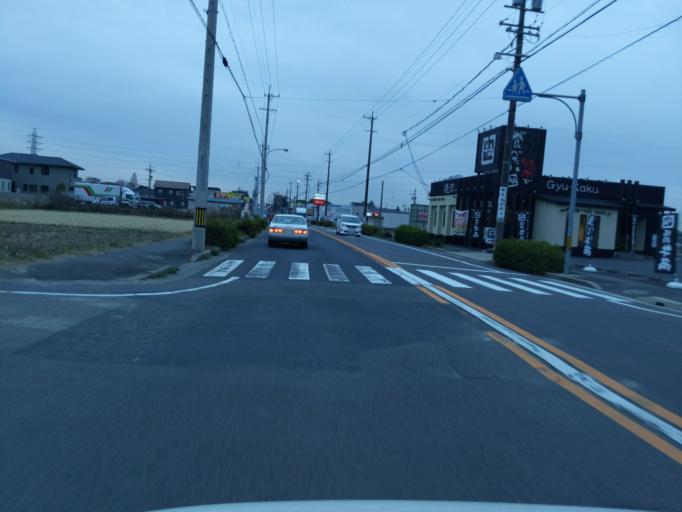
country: JP
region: Aichi
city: Kasugai
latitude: 35.2655
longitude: 136.9723
